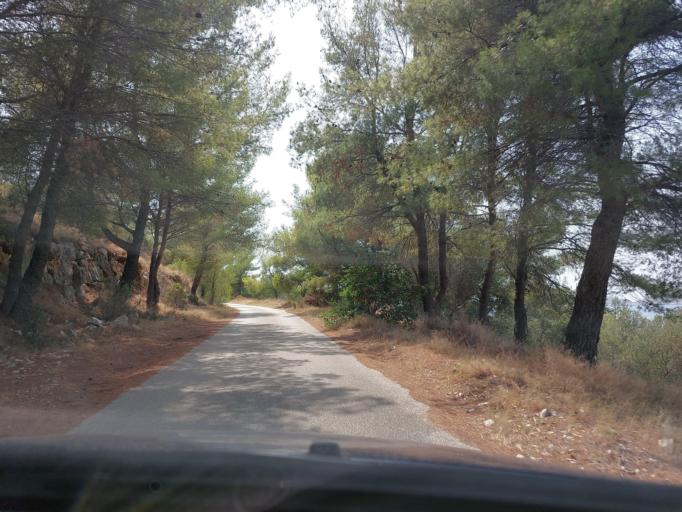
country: HR
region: Dubrovacko-Neretvanska
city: Smokvica
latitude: 42.7286
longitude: 16.8875
